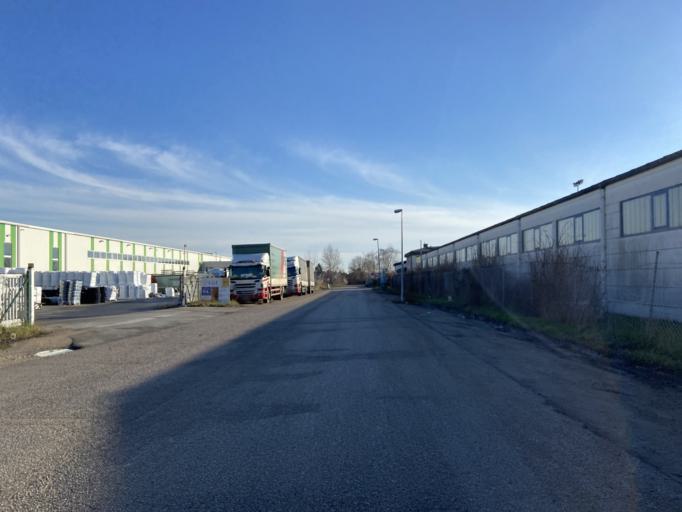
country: AT
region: Lower Austria
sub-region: Politischer Bezirk Modling
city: Neu-Guntramsdorf
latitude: 48.0614
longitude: 16.3276
